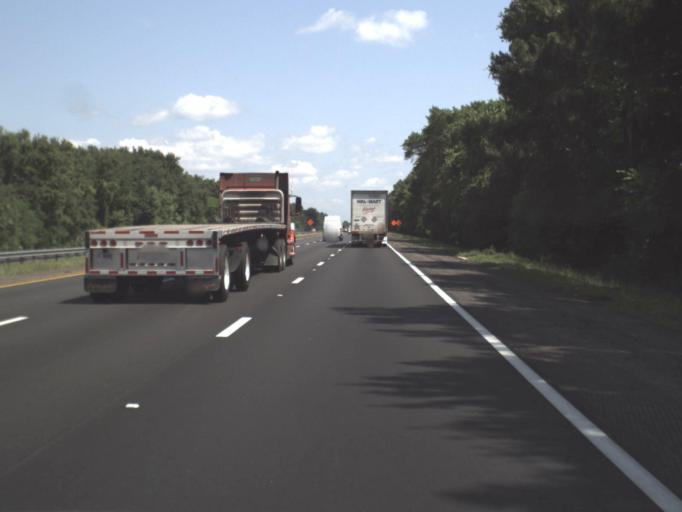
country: US
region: Florida
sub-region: Nassau County
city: Yulee
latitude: 30.5531
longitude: -81.6401
